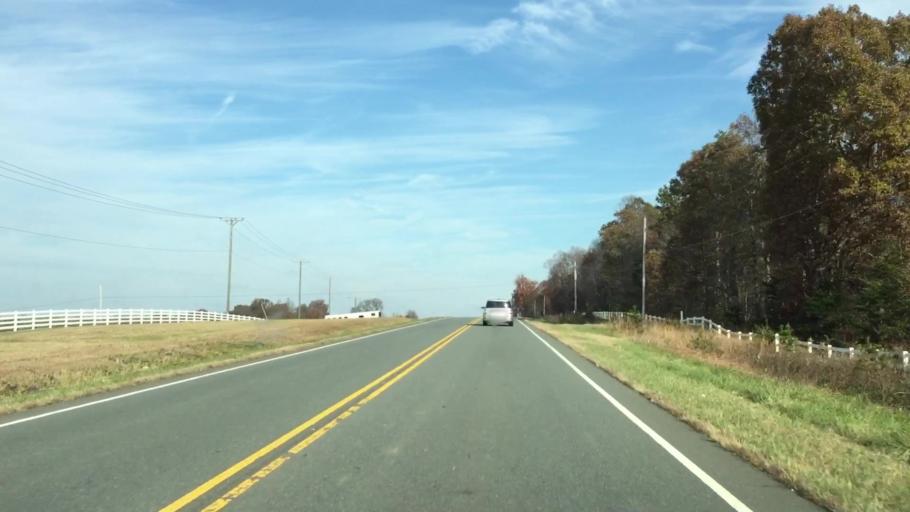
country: US
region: North Carolina
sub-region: Forsyth County
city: Walkertown
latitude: 36.1936
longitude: -80.0956
